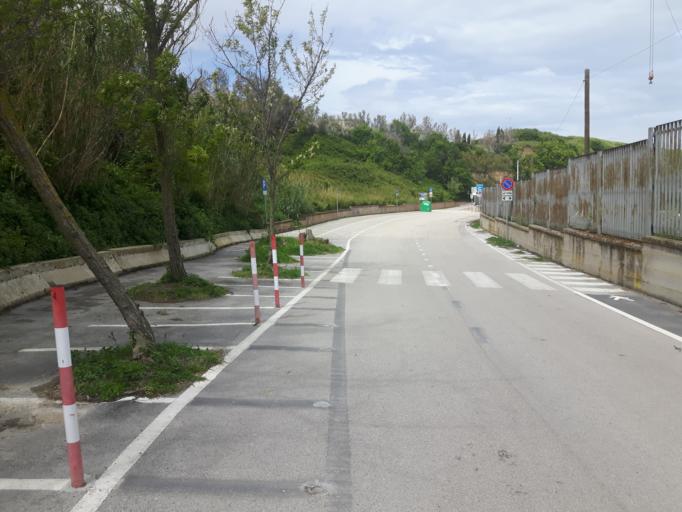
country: IT
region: Abruzzo
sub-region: Provincia di Chieti
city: Vasto
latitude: 42.1712
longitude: 14.7113
